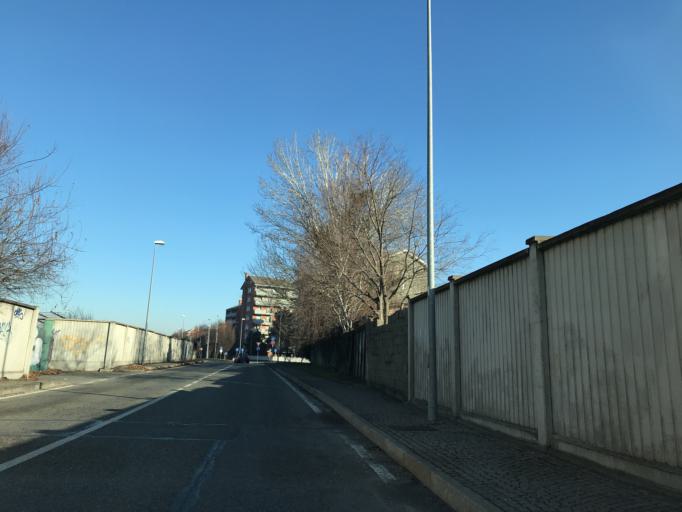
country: IT
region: Piedmont
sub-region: Provincia di Torino
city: Gerbido
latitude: 45.0400
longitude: 7.6147
